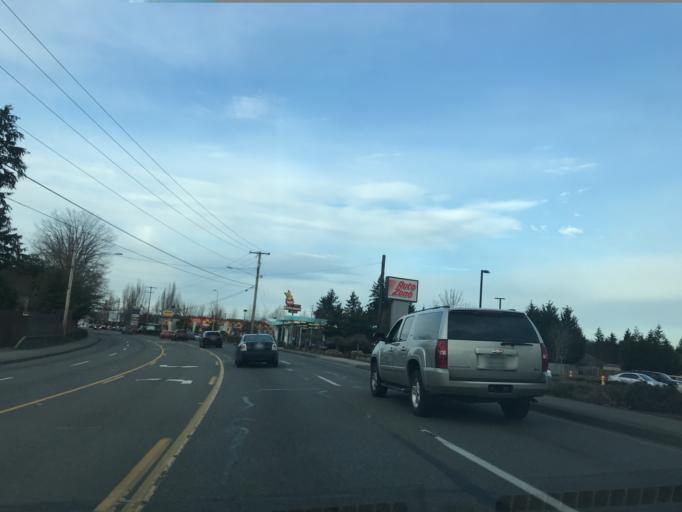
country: US
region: Washington
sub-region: King County
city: Auburn
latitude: 47.3173
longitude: -122.2218
